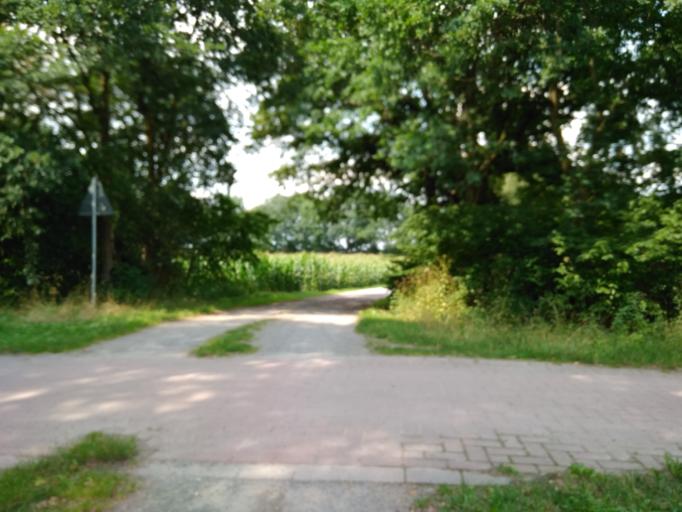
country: DE
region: North Rhine-Westphalia
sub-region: Regierungsbezirk Dusseldorf
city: Schermbeck
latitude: 51.6772
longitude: 6.9108
